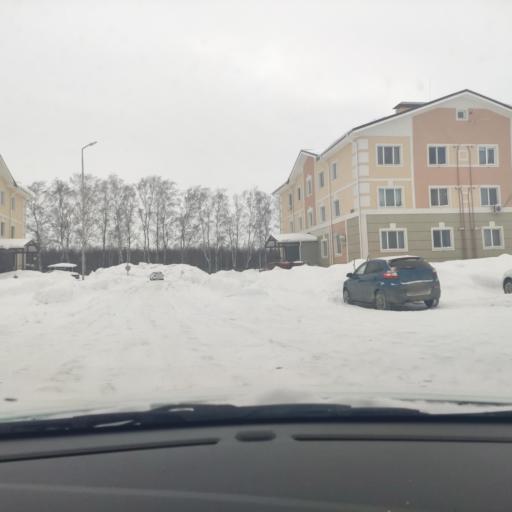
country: RU
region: Tatarstan
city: Stolbishchi
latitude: 55.7073
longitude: 49.3436
